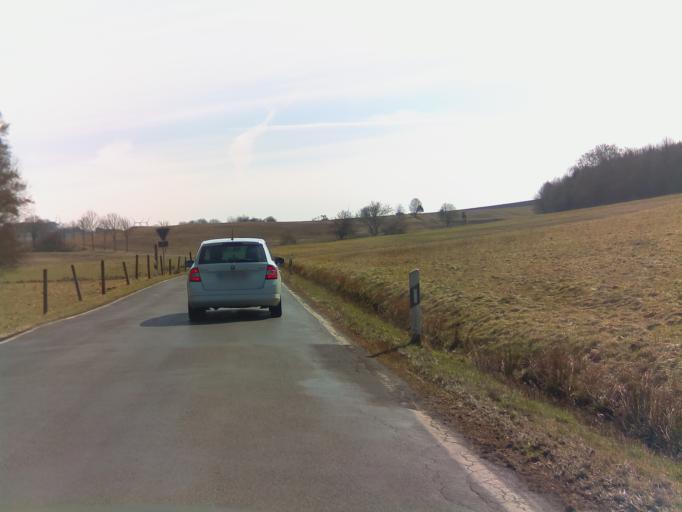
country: DE
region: Hesse
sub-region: Regierungsbezirk Giessen
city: Grunberg
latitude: 50.6304
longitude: 9.0483
